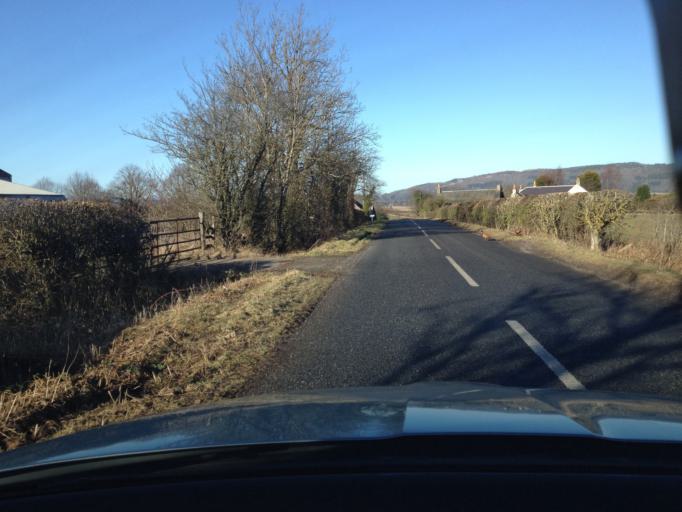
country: GB
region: Scotland
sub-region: Perth and Kinross
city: Bridge of Earn
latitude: 56.3250
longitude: -3.3763
